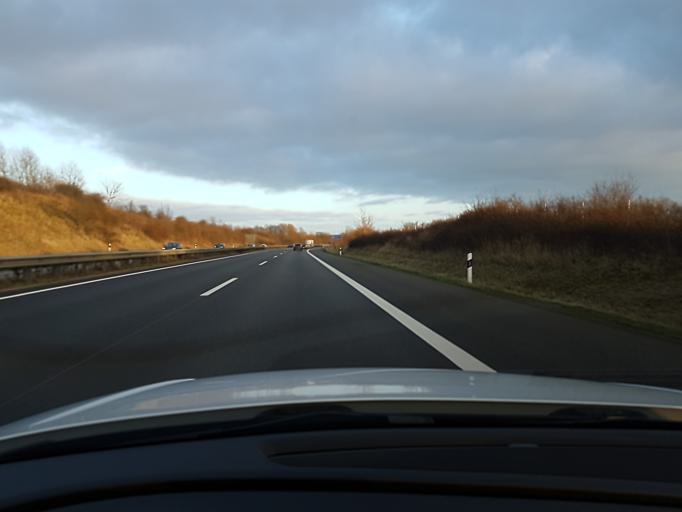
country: DE
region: Schleswig-Holstein
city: Hamberge
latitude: 53.8324
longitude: 10.6313
